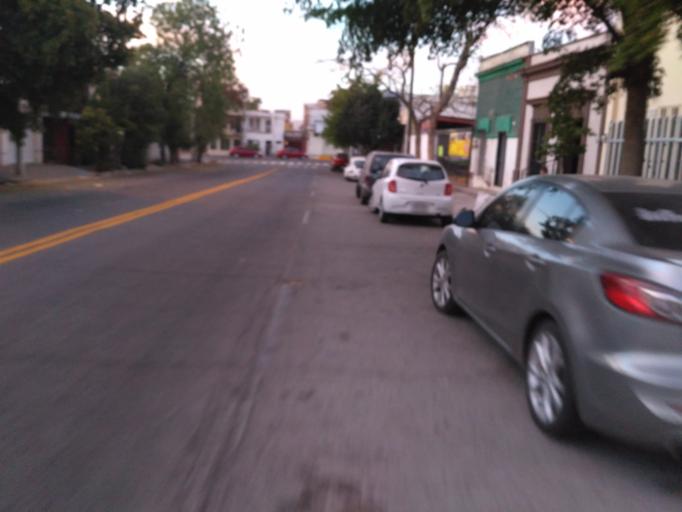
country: MX
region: Sinaloa
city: Culiacan
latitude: 24.8030
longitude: -107.4037
